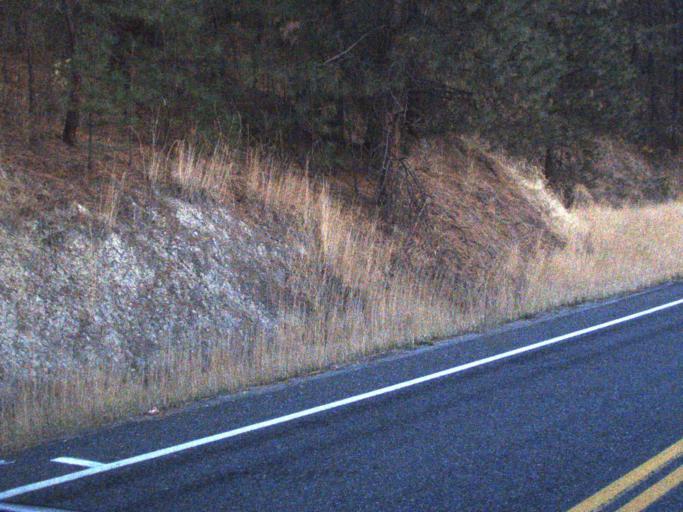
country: US
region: Washington
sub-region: Stevens County
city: Kettle Falls
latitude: 48.6265
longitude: -118.0729
